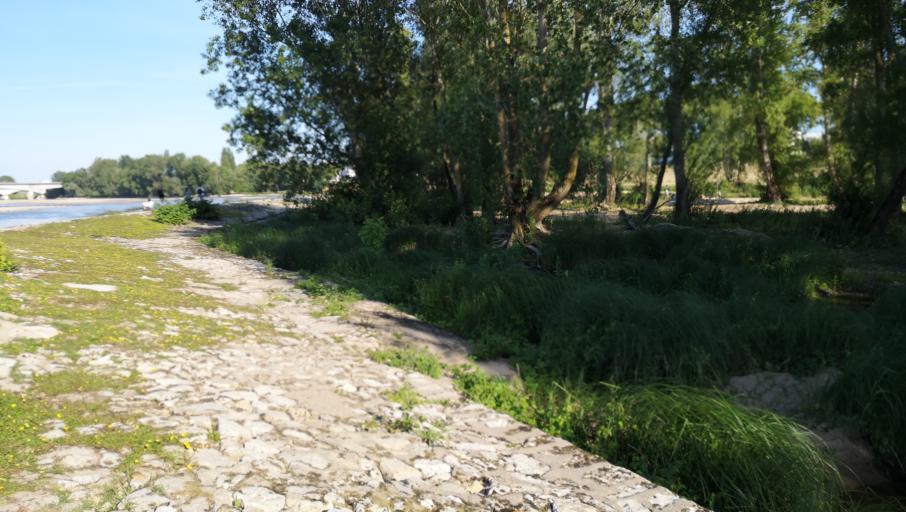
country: FR
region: Centre
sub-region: Departement du Loiret
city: Saint-Jean-le-Blanc
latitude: 47.8966
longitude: 1.9103
